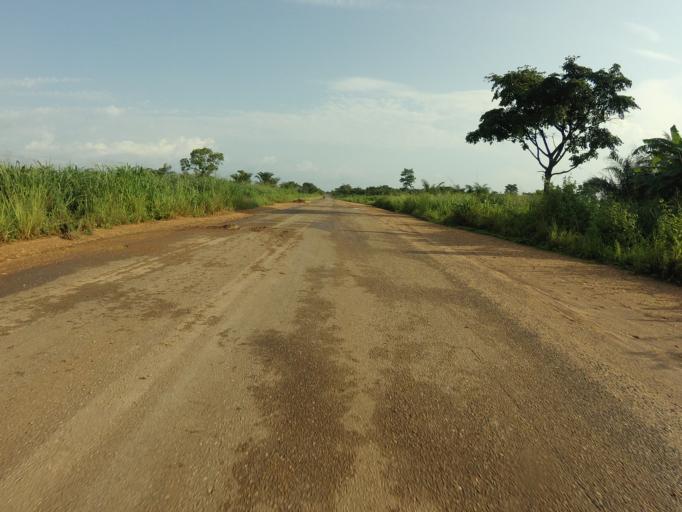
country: GH
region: Volta
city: Hohoe
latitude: 7.0718
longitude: 0.4355
